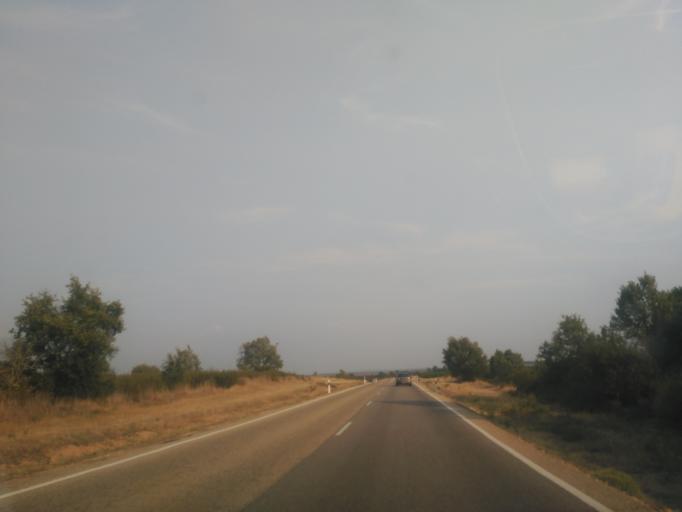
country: ES
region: Castille and Leon
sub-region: Provincia de Zamora
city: Tabara
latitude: 41.8630
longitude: -5.9989
